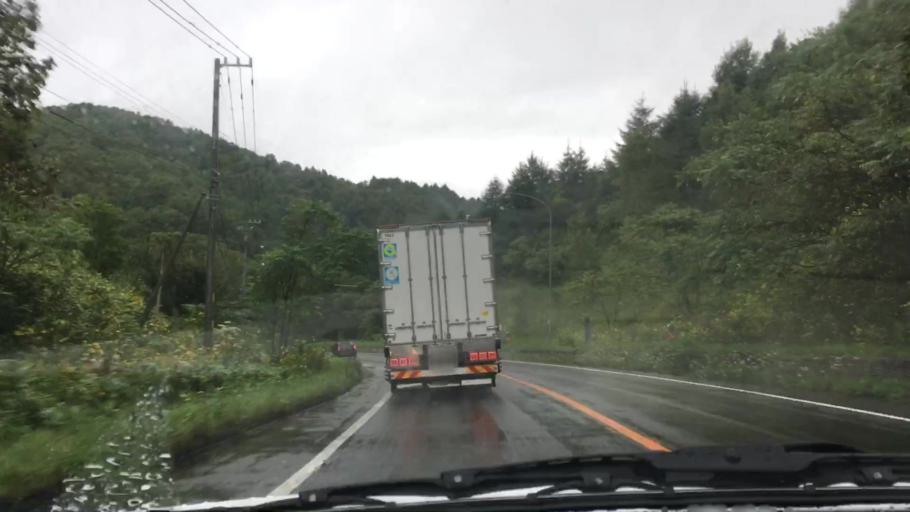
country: JP
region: Hokkaido
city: Niseko Town
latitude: 42.5966
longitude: 140.6736
